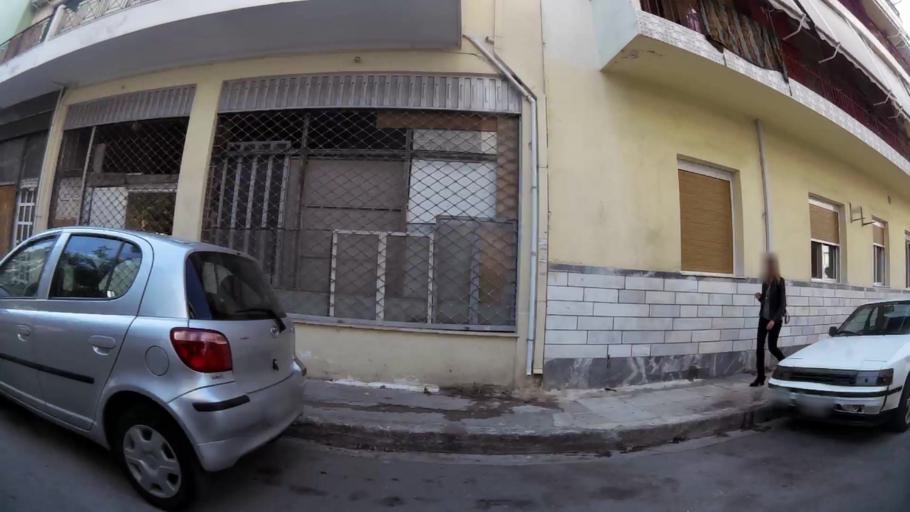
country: GR
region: Attica
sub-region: Nomos Piraios
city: Nikaia
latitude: 37.9621
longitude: 23.6472
